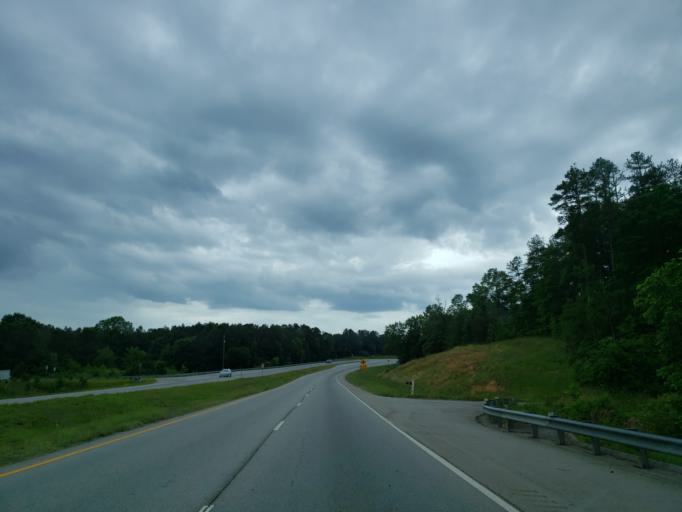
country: US
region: Georgia
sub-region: Polk County
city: Cedartown
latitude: 34.0030
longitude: -85.2238
